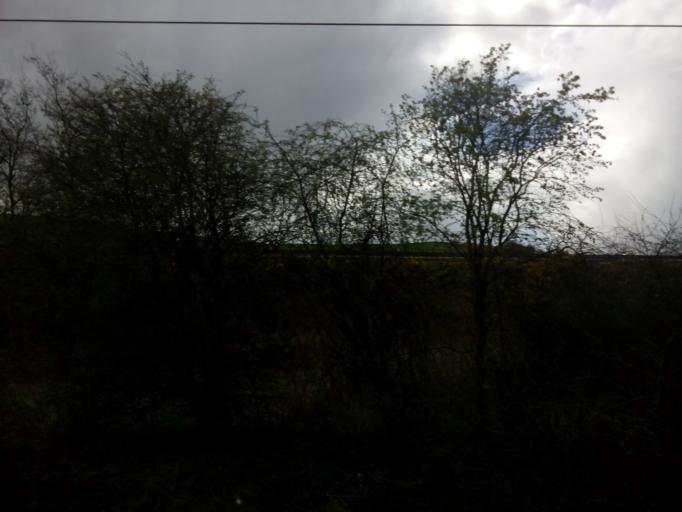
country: GB
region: Scotland
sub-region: The Scottish Borders
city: Duns
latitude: 55.8946
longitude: -2.3290
